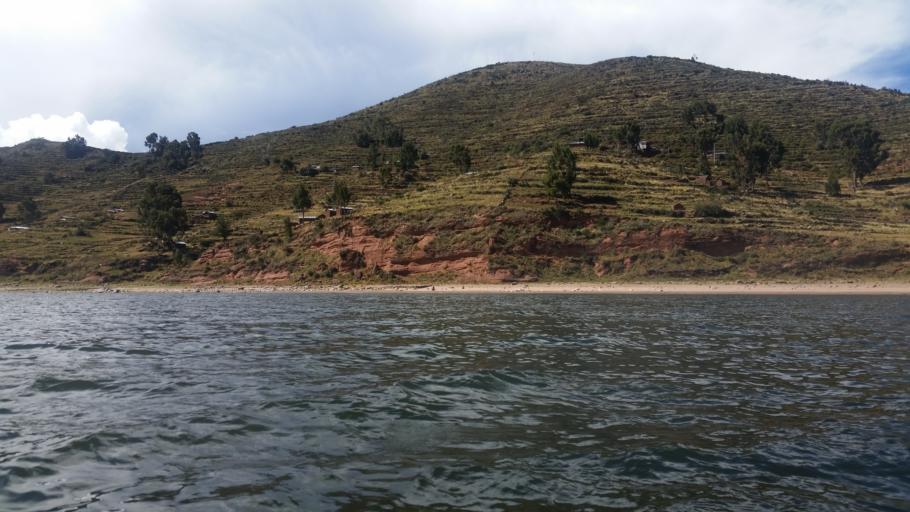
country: PE
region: Puno
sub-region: Provincia de Puno
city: Taquile
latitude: -15.7299
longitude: -69.7584
